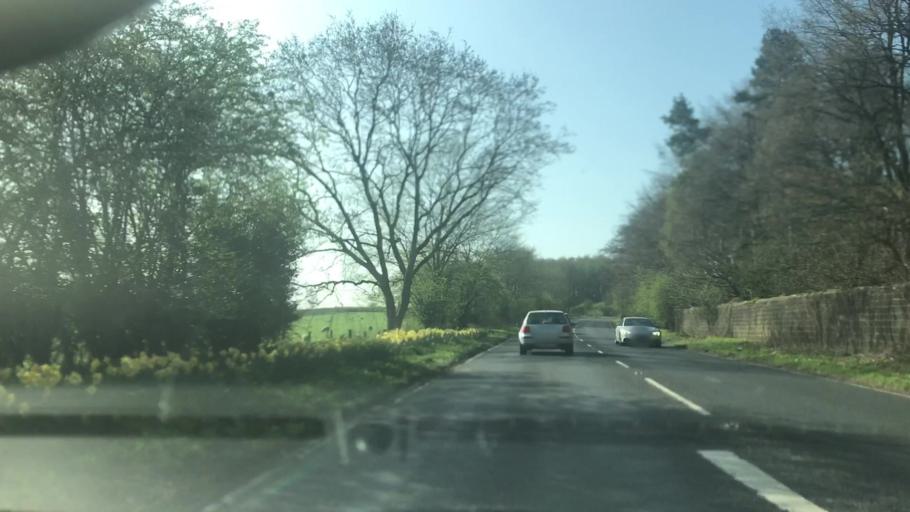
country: GB
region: England
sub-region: City and Borough of Leeds
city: Shadwell
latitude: 53.8869
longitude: -1.5080
